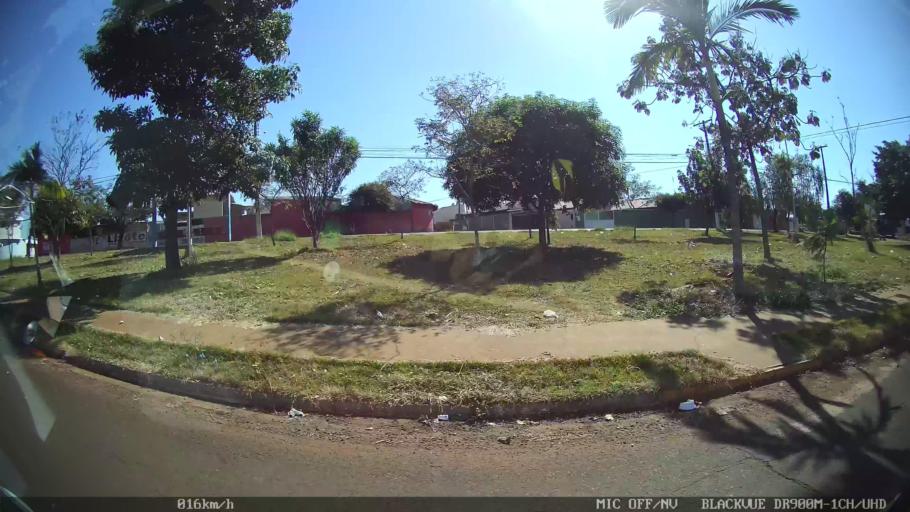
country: BR
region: Sao Paulo
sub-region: Batatais
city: Batatais
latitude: -20.8860
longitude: -47.5718
